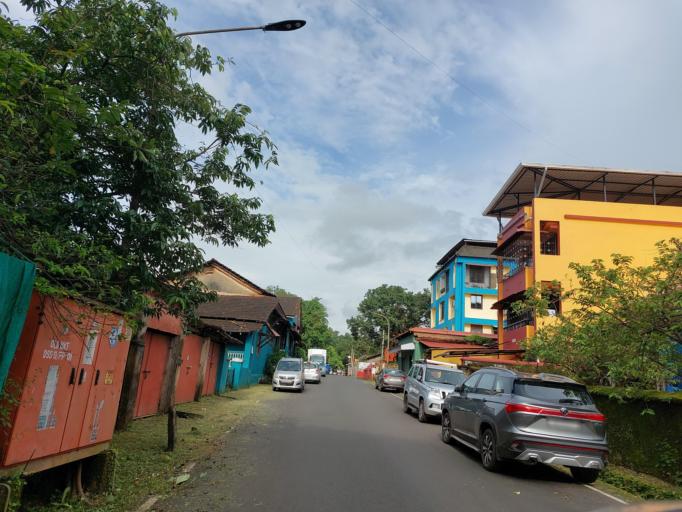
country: IN
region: Goa
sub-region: South Goa
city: Madgaon
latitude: 15.2790
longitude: 73.9554
